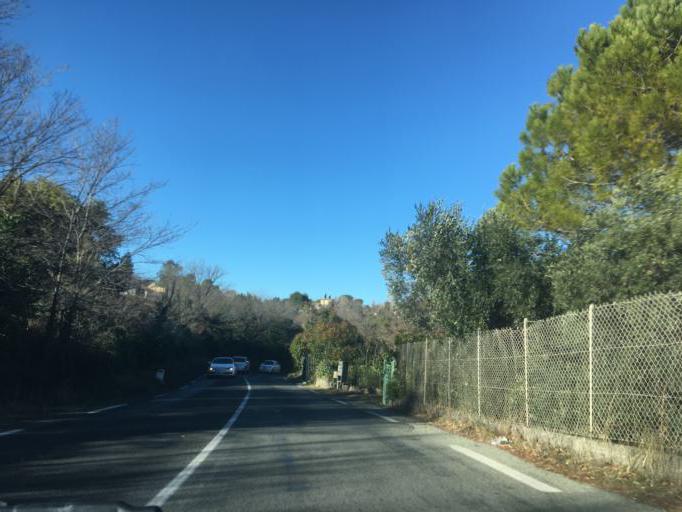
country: FR
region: Provence-Alpes-Cote d'Azur
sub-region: Departement du Var
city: Flayosc
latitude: 43.5365
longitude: 6.3986
